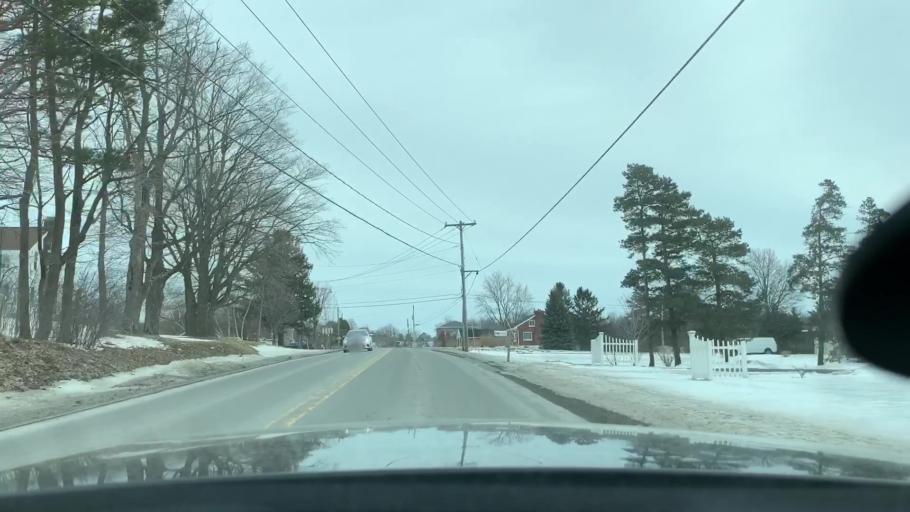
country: US
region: New York
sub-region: Oneida County
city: Washington Mills
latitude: 43.0496
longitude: -75.2346
